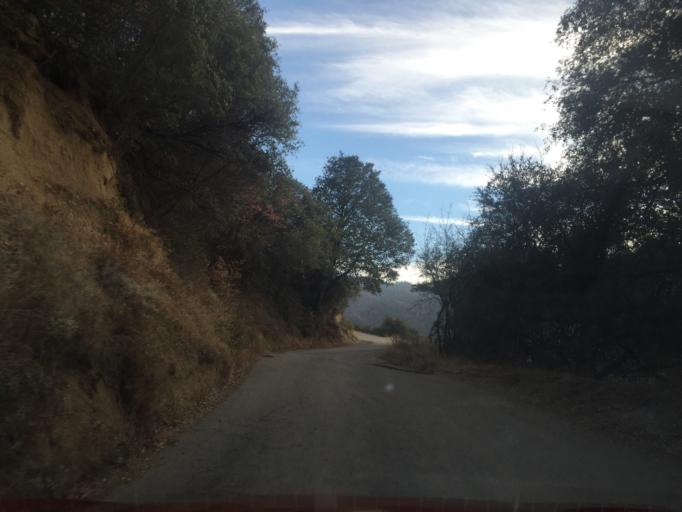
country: US
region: California
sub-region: Tulare County
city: Three Rivers
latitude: 36.4332
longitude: -118.7642
